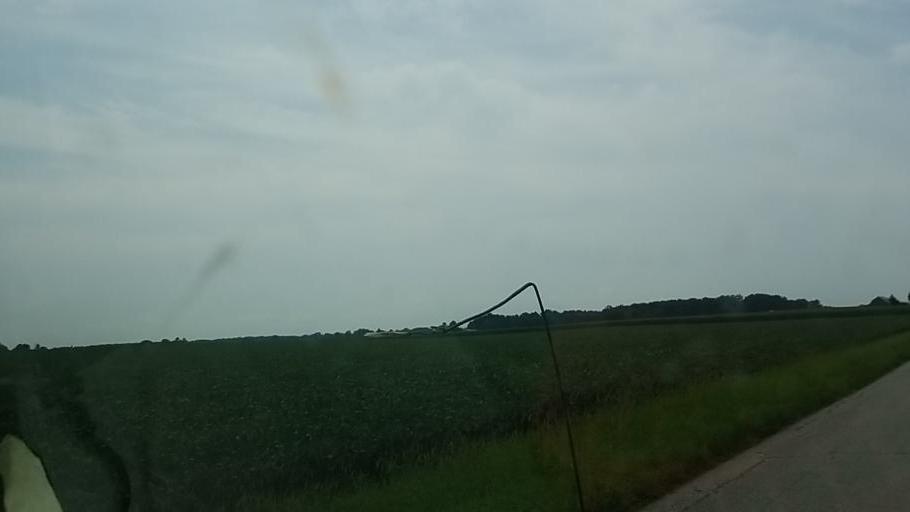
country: US
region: Ohio
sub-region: Morrow County
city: Cardington
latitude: 40.6161
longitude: -82.9549
